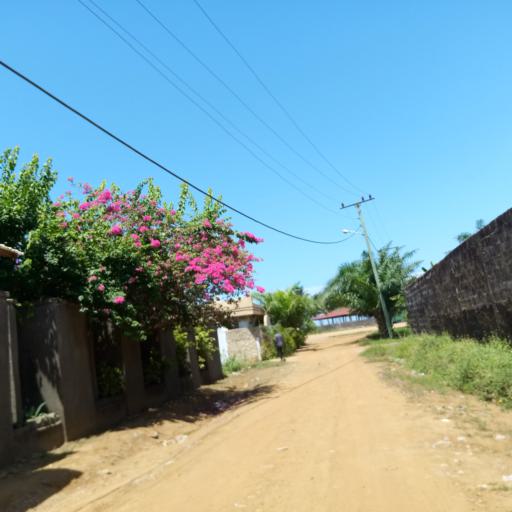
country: LR
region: Montserrado
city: Monrovia
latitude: 6.2343
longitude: -10.6932
